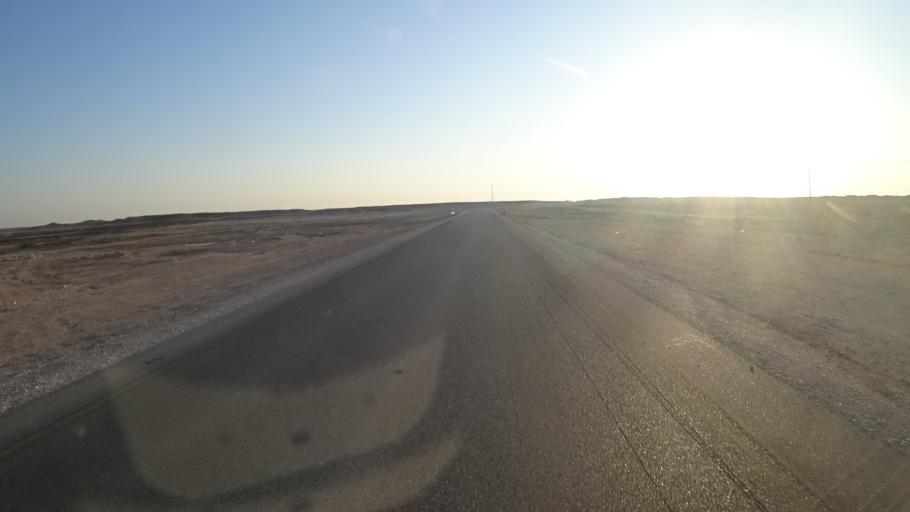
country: OM
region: Zufar
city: Salalah
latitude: 17.5461
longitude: 53.4236
